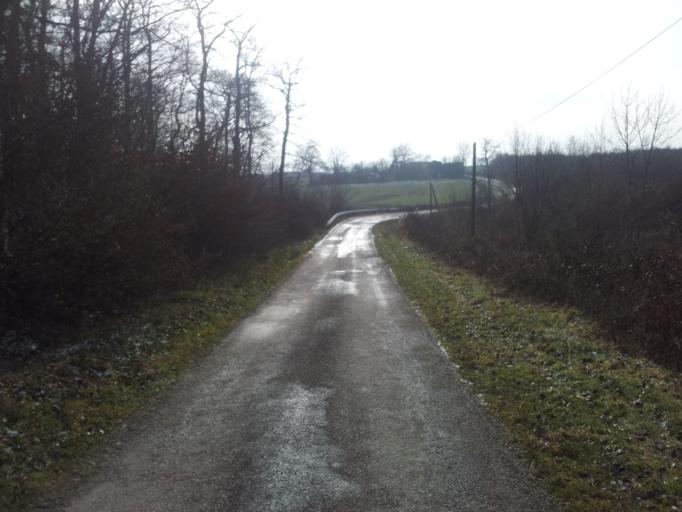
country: FR
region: Auvergne
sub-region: Departement de l'Allier
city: Chantelle
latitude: 46.3174
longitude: 3.0888
